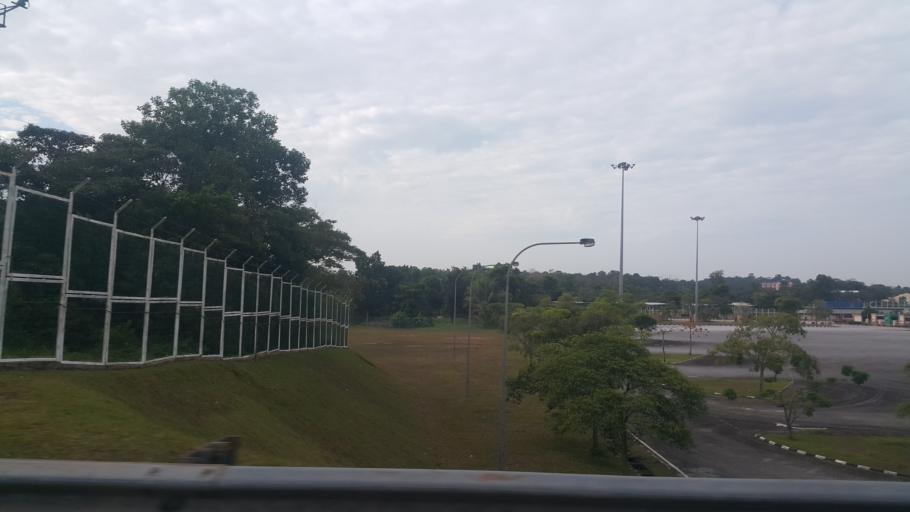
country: MY
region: Johor
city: Pekan Nenas
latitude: 1.3760
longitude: 103.6030
